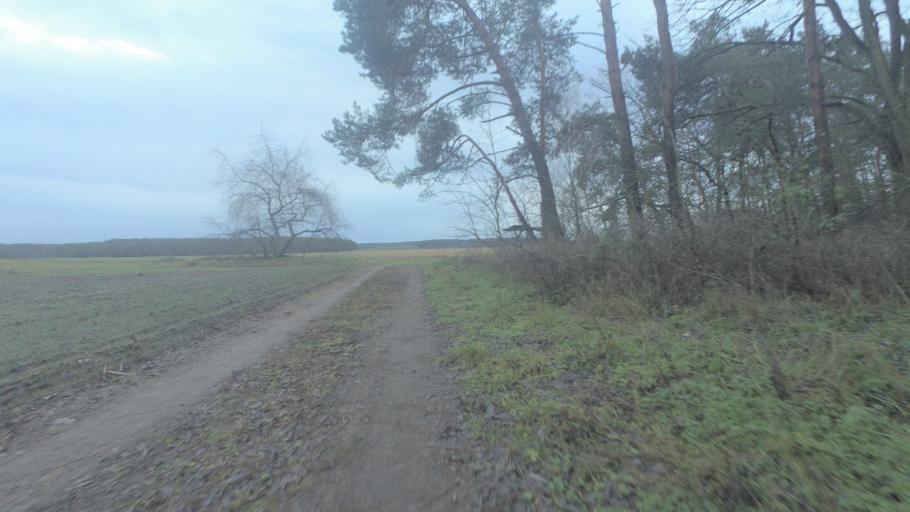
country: DE
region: Brandenburg
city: Ludwigsfelde
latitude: 52.2662
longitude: 13.2378
